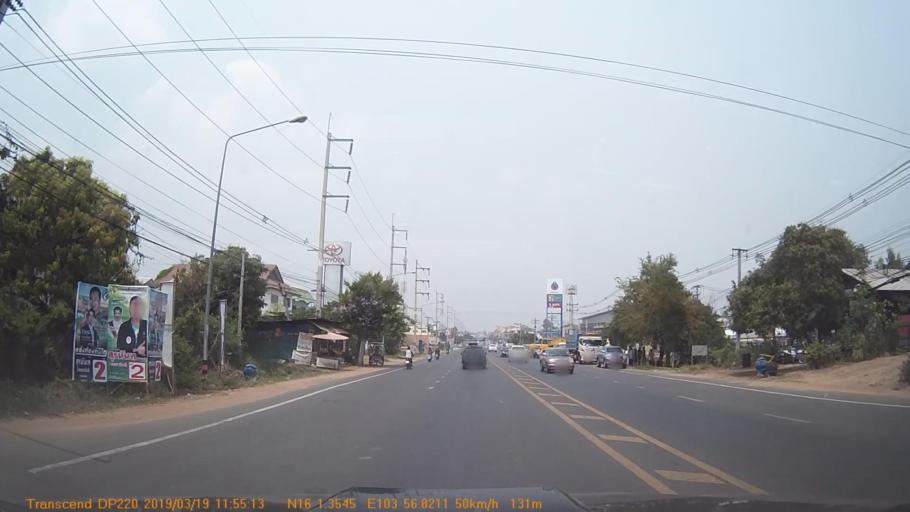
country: TH
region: Roi Et
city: Ban Selaphum
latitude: 16.0226
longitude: 103.9470
